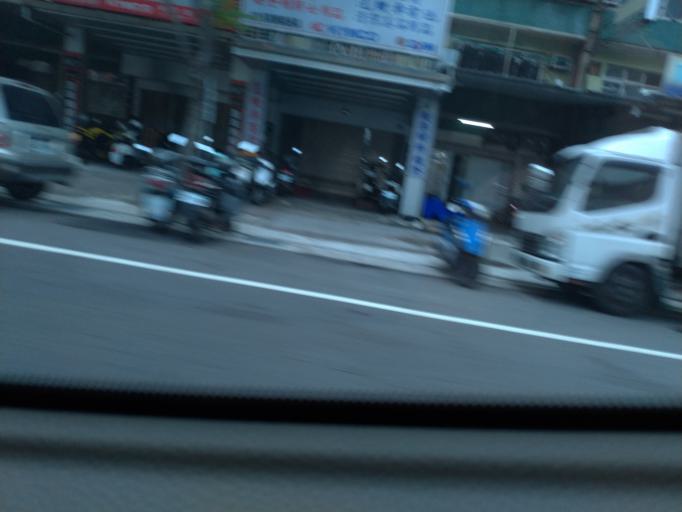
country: TW
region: Taiwan
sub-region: Taoyuan
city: Taoyuan
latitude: 24.9307
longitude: 121.3778
